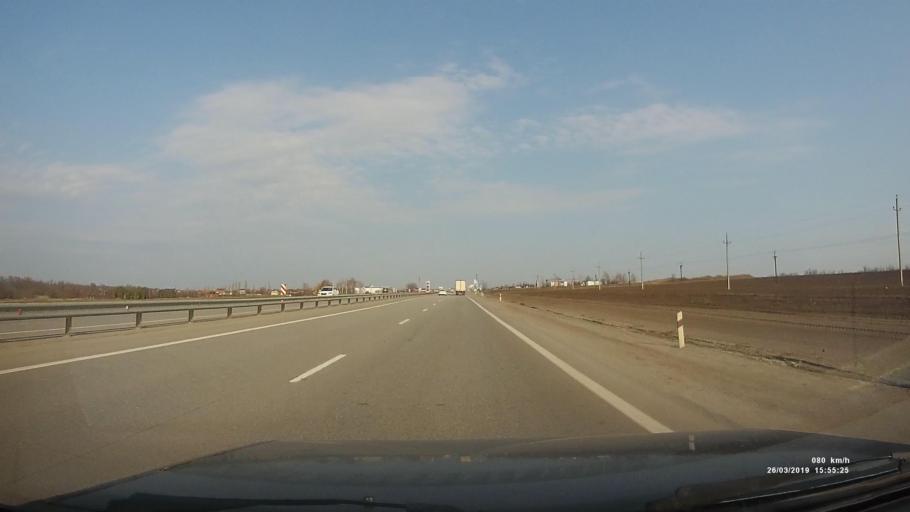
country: RU
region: Rostov
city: Kalinin
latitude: 47.2664
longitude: 39.5752
